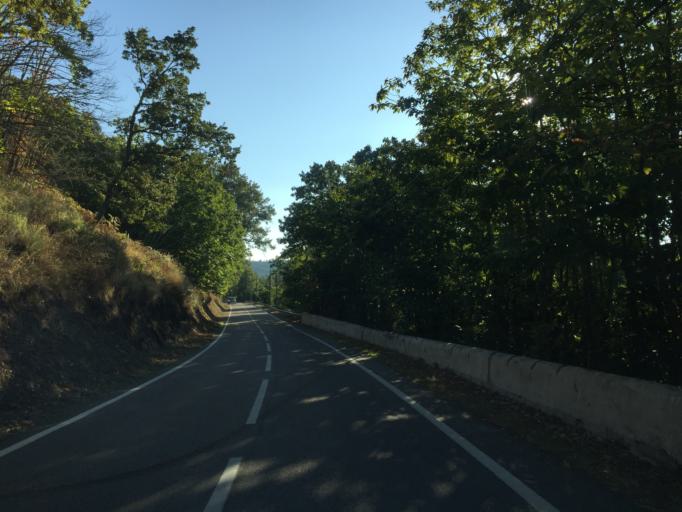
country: PT
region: Portalegre
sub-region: Marvao
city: Marvao
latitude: 39.4031
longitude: -7.3872
